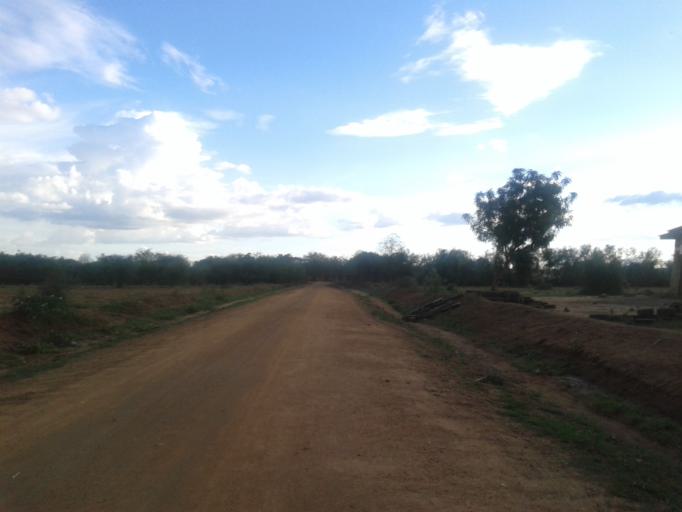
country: UG
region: Northern Region
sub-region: Kotido District
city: Kotido
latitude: 2.9991
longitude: 34.1048
